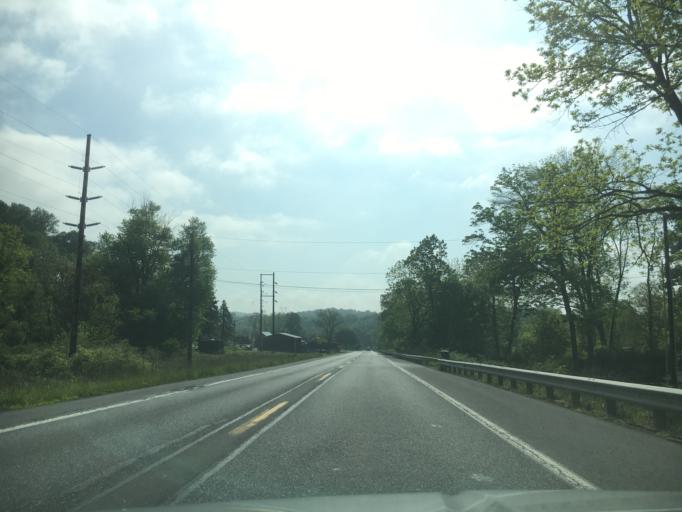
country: US
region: Pennsylvania
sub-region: Berks County
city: New Berlinville
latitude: 40.3625
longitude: -75.6778
